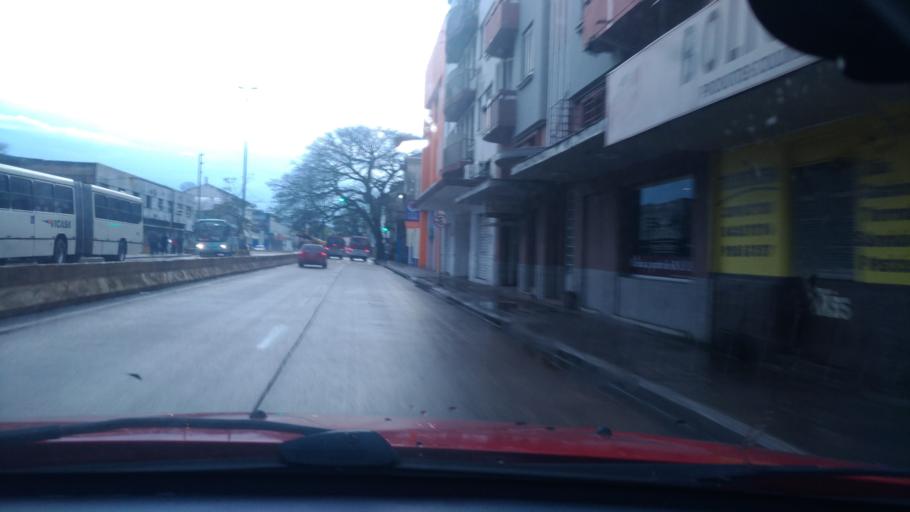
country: BR
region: Rio Grande do Sul
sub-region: Porto Alegre
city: Porto Alegre
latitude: -30.0248
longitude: -51.2146
